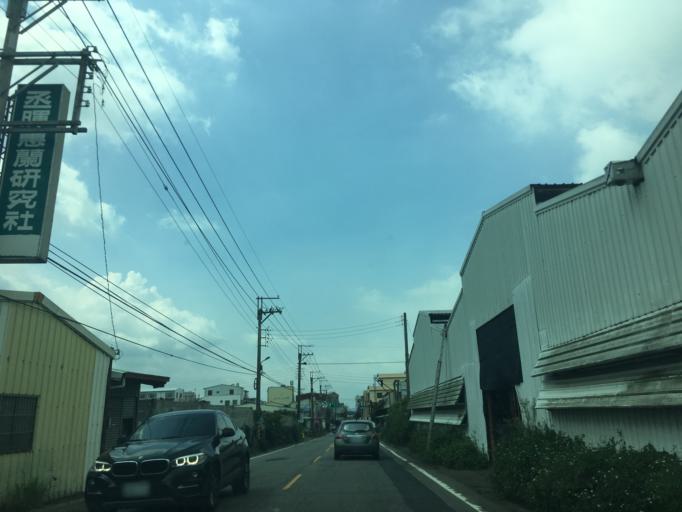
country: TW
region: Taiwan
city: Fengyuan
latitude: 24.2158
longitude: 120.7959
